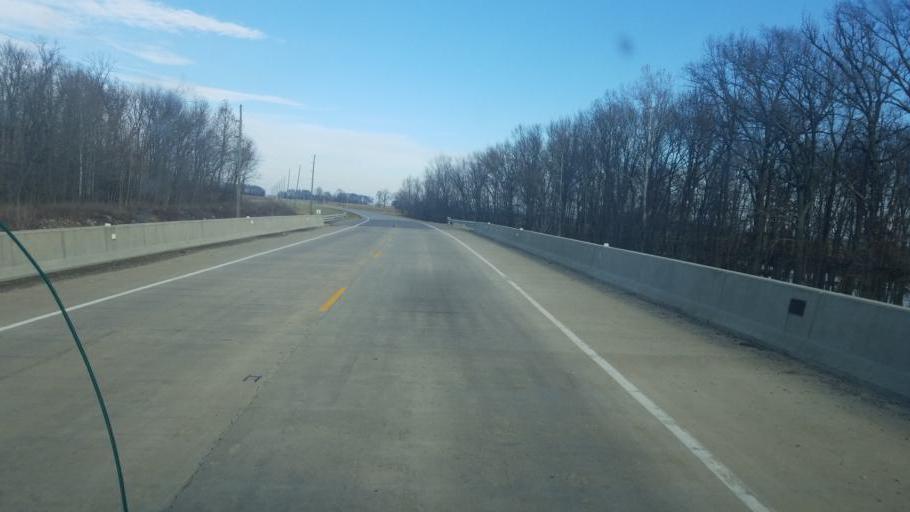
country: US
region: Illinois
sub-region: White County
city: Carmi
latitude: 38.1088
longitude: -88.1239
